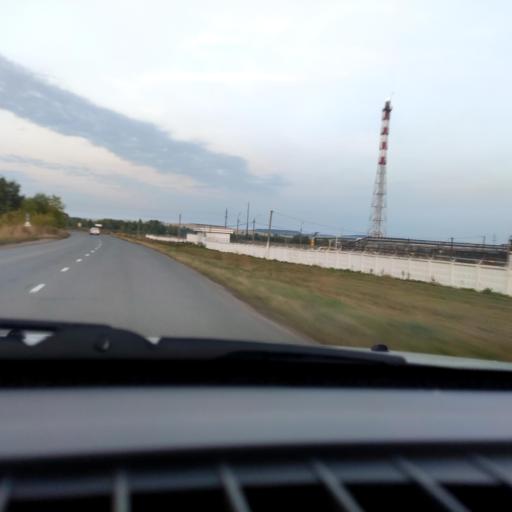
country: RU
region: Perm
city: Gamovo
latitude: 57.9045
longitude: 56.1339
